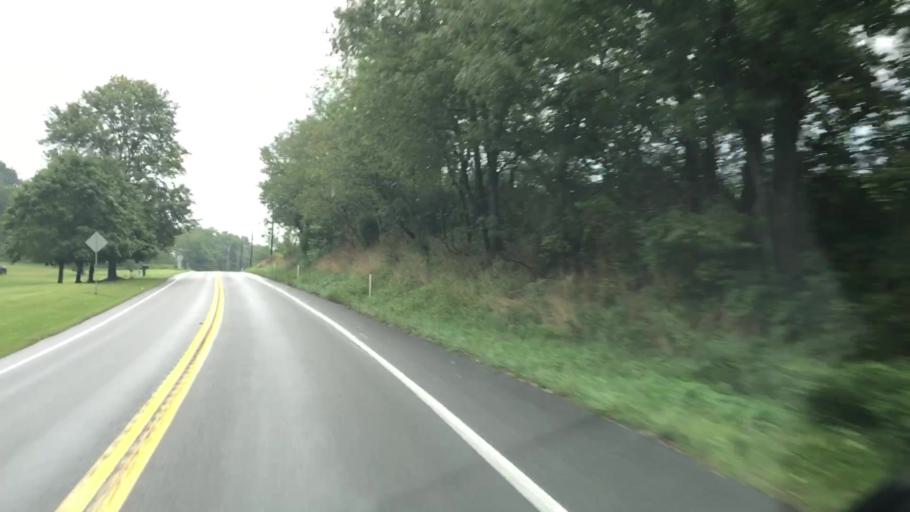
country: US
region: Pennsylvania
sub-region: Perry County
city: New Bloomfield
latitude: 40.3761
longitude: -77.1531
